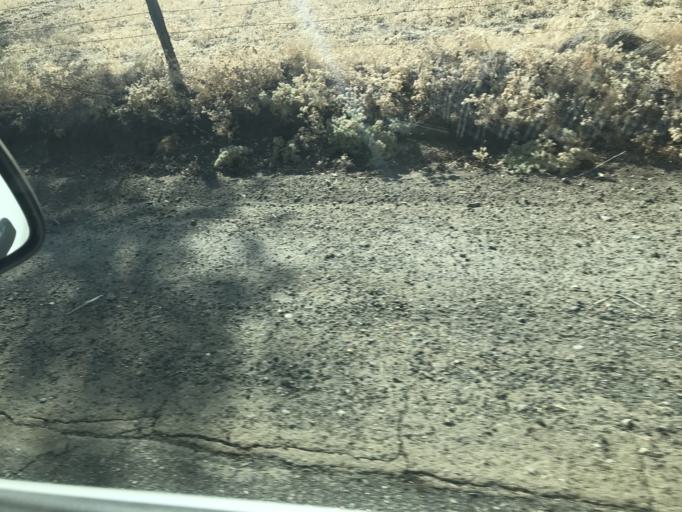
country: US
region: California
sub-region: Fresno County
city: Minkler
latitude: 36.8951
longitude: -119.4635
